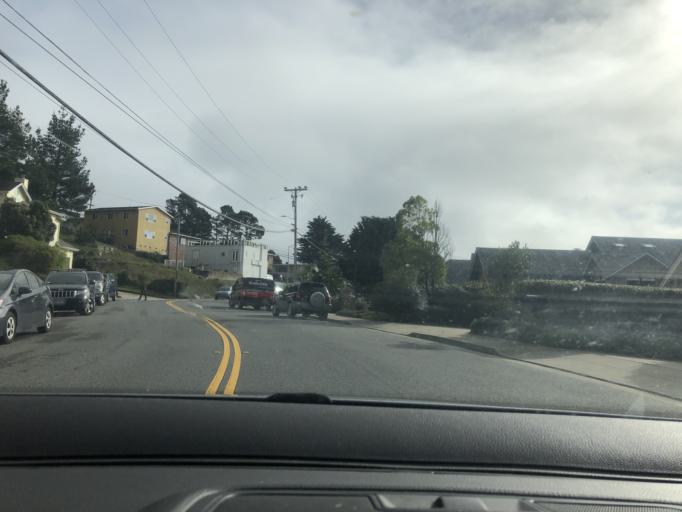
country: US
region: California
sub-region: San Mateo County
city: Pacifica
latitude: 37.6471
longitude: -122.4782
